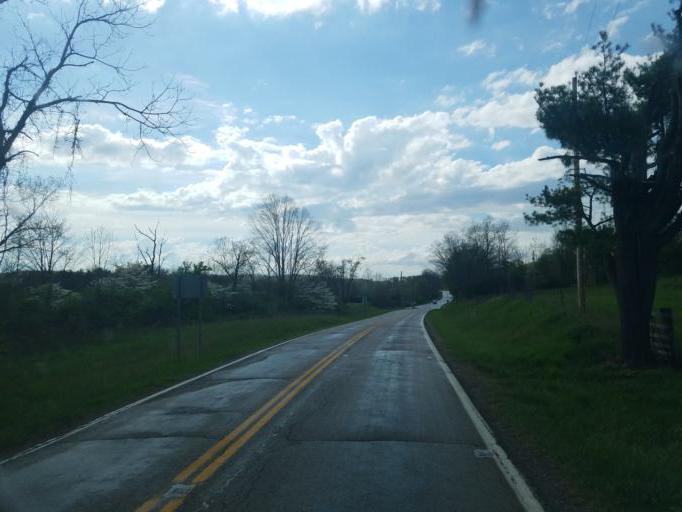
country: US
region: Ohio
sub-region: Knox County
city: Oak Hill
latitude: 40.3882
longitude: -82.2568
